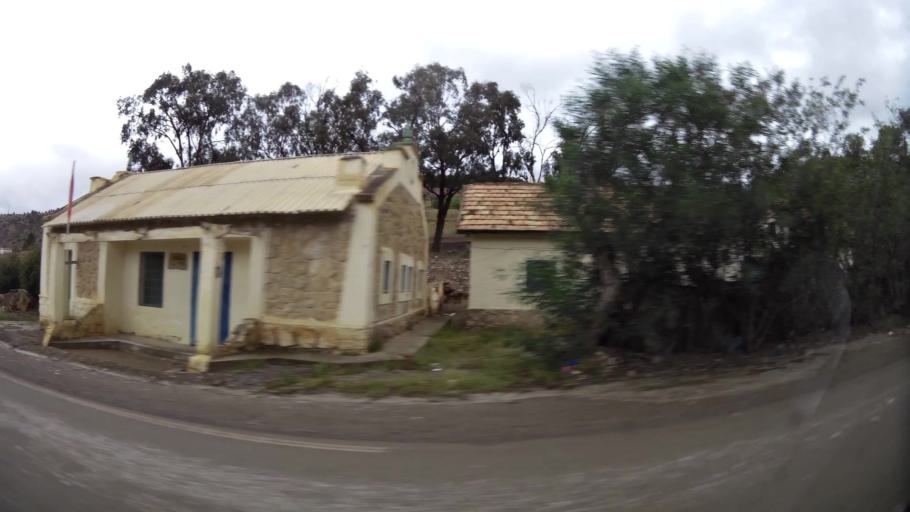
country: MA
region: Taza-Al Hoceima-Taounate
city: Imzourene
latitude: 34.9634
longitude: -3.8123
